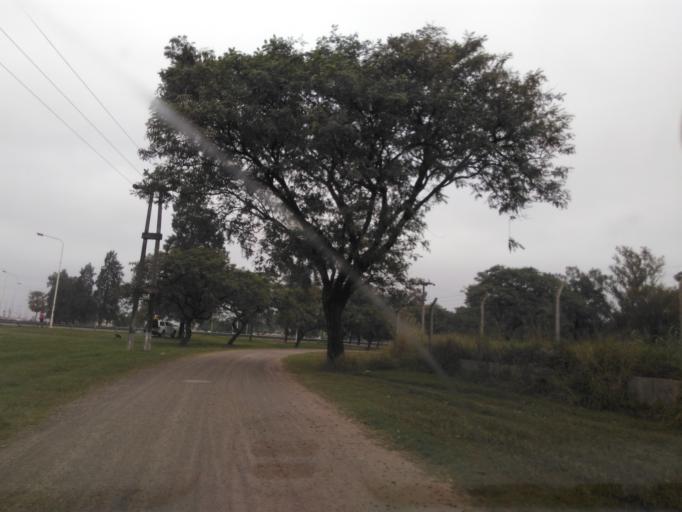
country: AR
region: Chaco
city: Fontana
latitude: -27.4441
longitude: -59.0220
